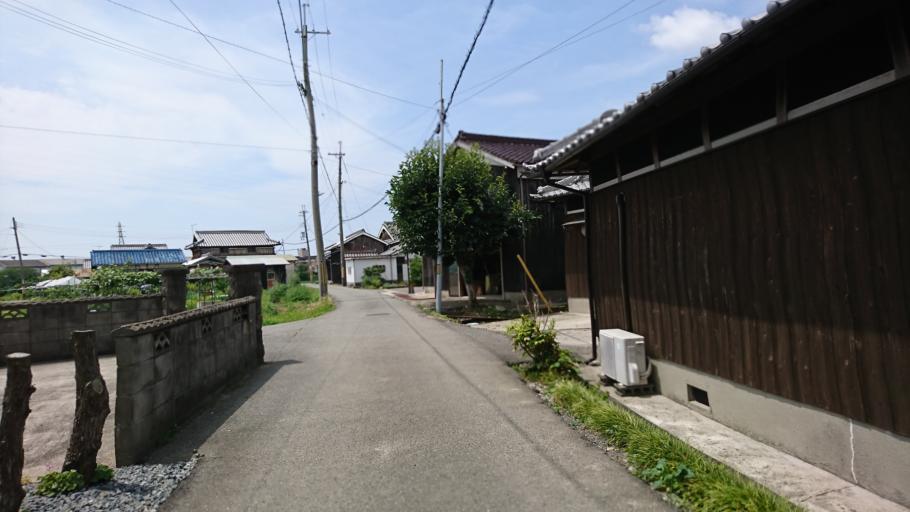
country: JP
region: Hyogo
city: Kakogawacho-honmachi
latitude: 34.7301
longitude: 134.9110
